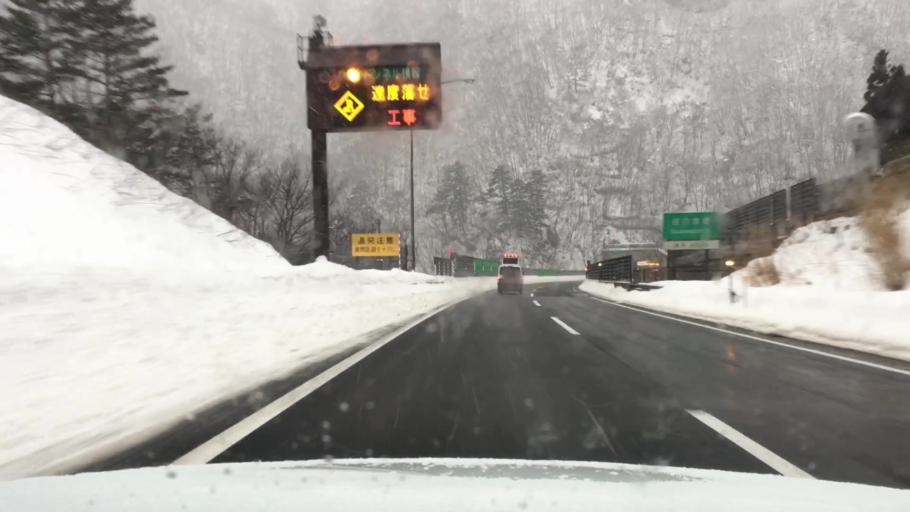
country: JP
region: Akita
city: Hanawa
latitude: 40.1264
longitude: 140.8235
